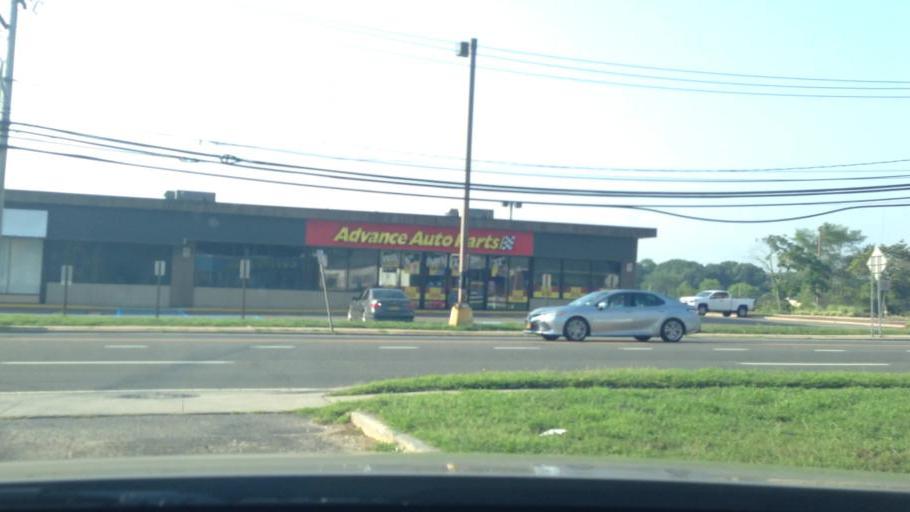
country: US
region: New York
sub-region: Suffolk County
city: Coram
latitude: 40.8709
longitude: -72.9981
